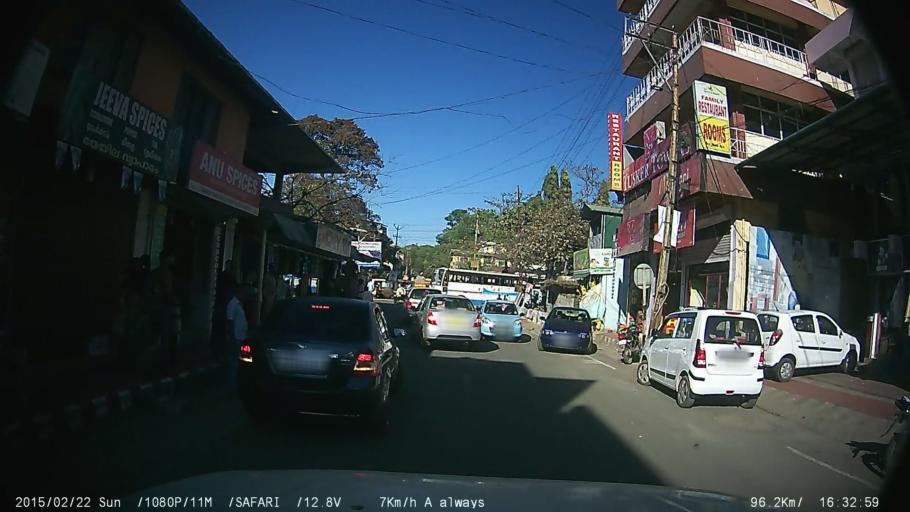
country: IN
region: Tamil Nadu
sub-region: Theni
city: Gudalur
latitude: 9.6084
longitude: 77.1688
